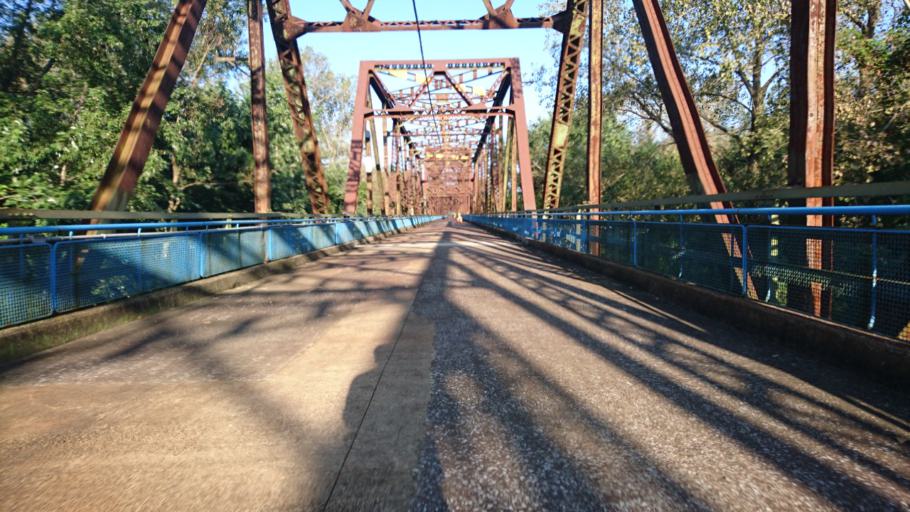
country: US
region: Missouri
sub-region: Saint Louis County
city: Glasgow Village
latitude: 38.7575
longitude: -90.1663
